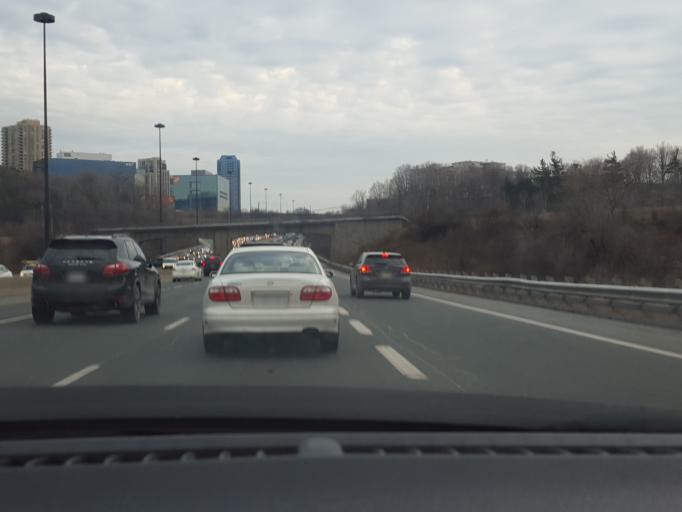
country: CA
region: Ontario
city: Willowdale
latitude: 43.7357
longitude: -79.3320
